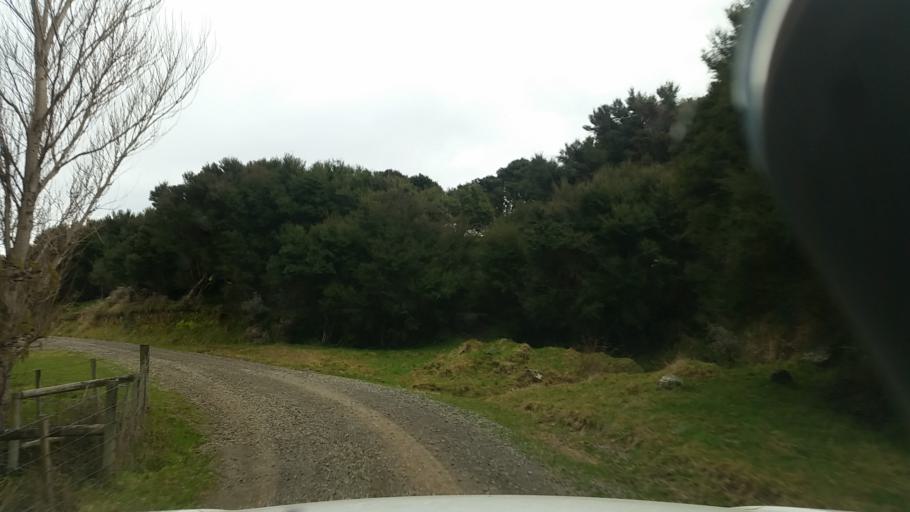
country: NZ
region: Canterbury
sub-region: Christchurch City
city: Christchurch
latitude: -43.8584
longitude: 173.0227
